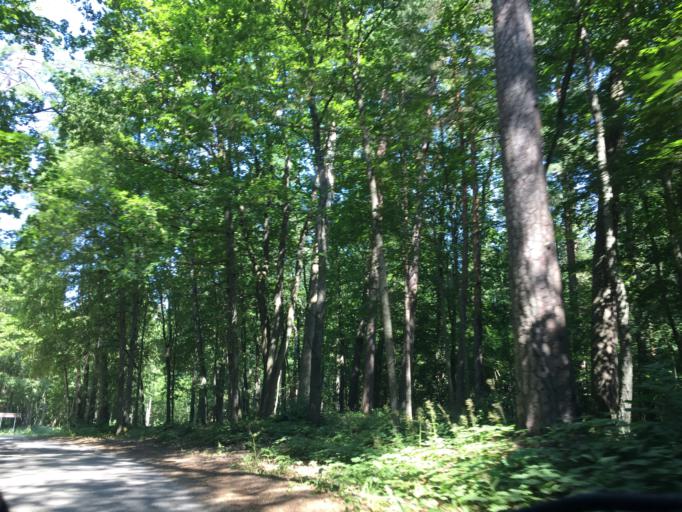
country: LV
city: Tervete
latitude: 56.4818
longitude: 23.3977
